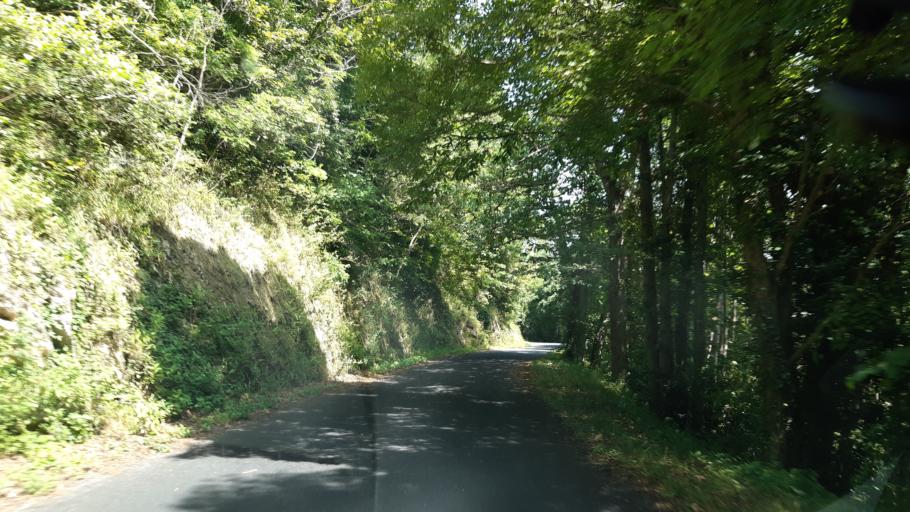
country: FR
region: Languedoc-Roussillon
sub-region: Departement des Pyrenees-Orientales
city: Arles
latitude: 42.5213
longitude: 2.6175
